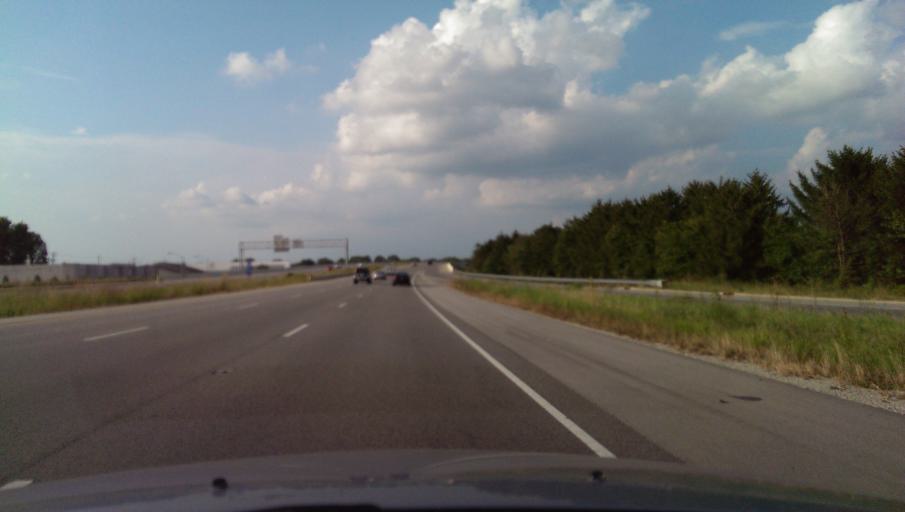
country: US
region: Indiana
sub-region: Hamilton County
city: Westfield
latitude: 40.0453
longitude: -86.1356
